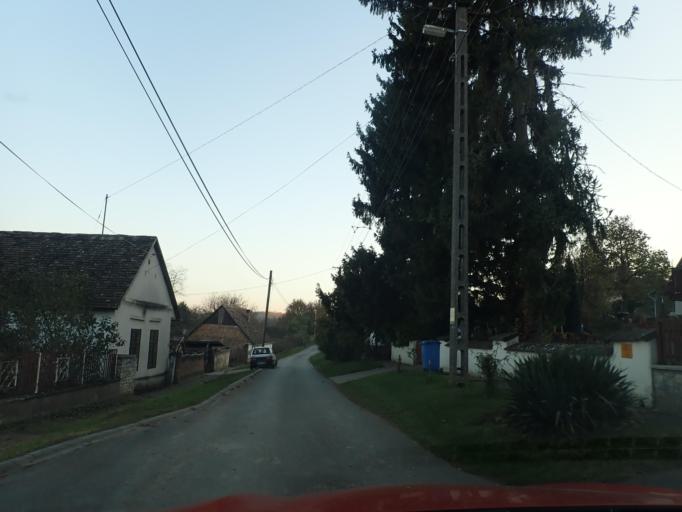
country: HU
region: Baranya
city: Kozarmisleny
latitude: 46.0344
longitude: 18.3868
